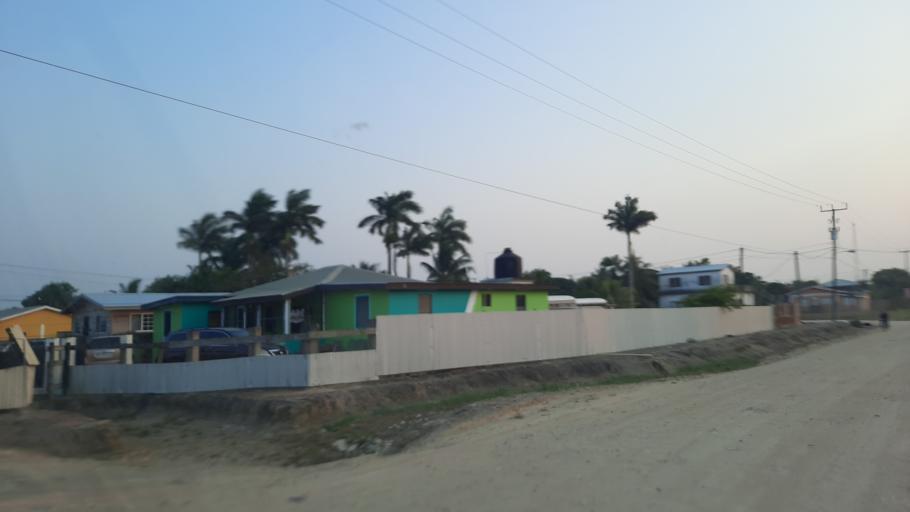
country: BZ
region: Stann Creek
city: Placencia
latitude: 16.5343
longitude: -88.4265
